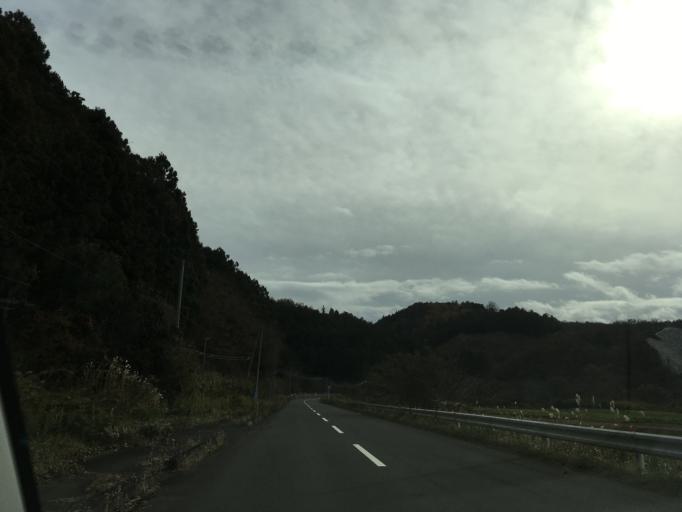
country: JP
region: Iwate
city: Ichinoseki
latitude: 38.7531
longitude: 141.2847
